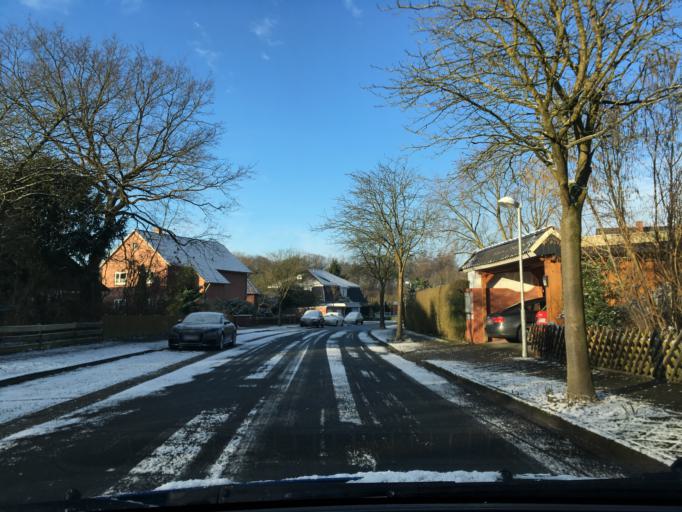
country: DE
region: Lower Saxony
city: Lueneburg
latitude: 53.2317
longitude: 10.4201
